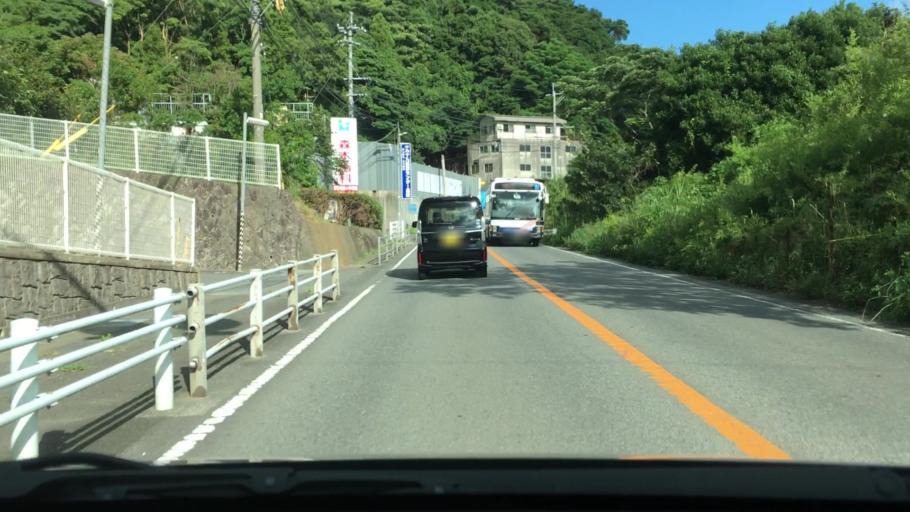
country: JP
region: Nagasaki
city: Togitsu
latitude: 32.8095
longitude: 129.8114
